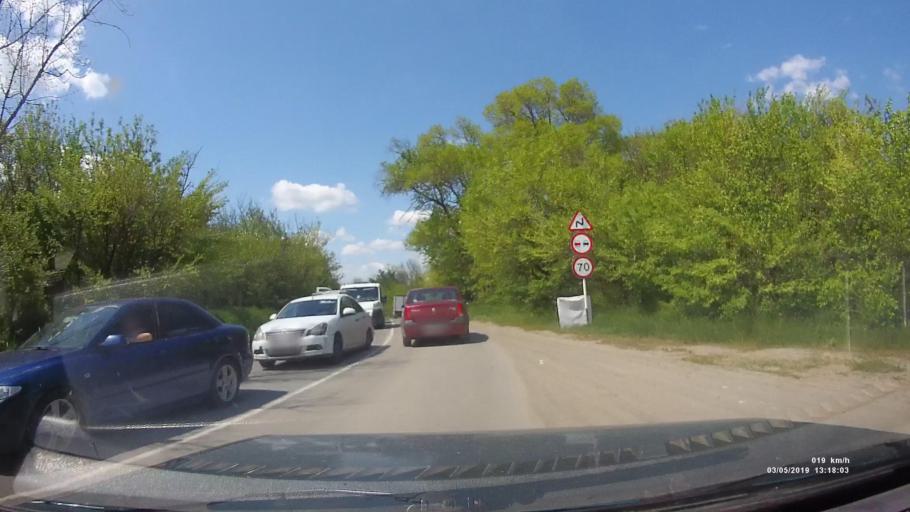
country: RU
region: Rostov
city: Semikarakorsk
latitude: 47.5309
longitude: 40.7505
